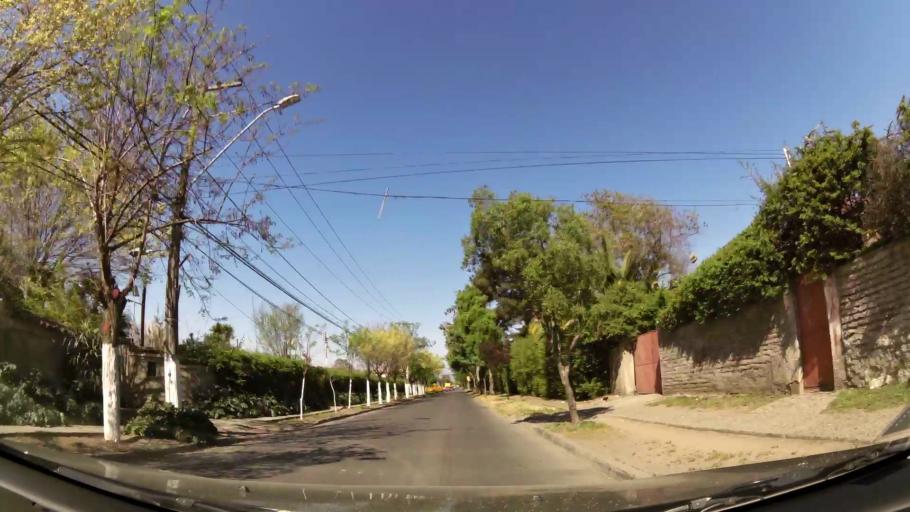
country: CL
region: Santiago Metropolitan
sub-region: Provincia de Maipo
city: San Bernardo
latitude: -33.6097
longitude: -70.7061
